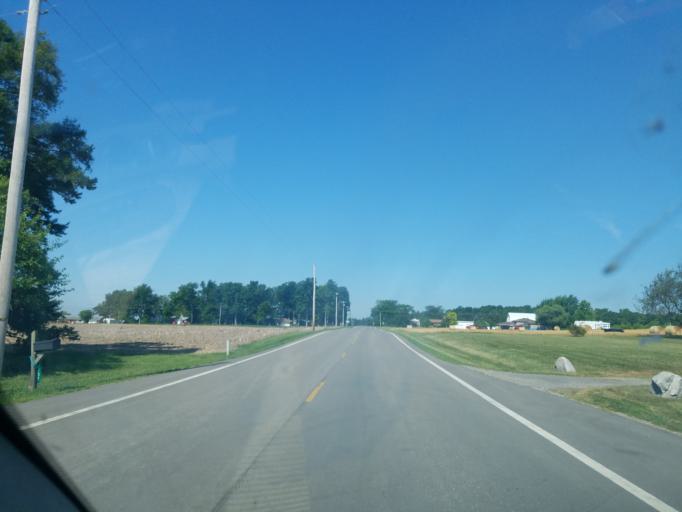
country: US
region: Ohio
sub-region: Logan County
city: Northwood
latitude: 40.4521
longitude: -83.7561
